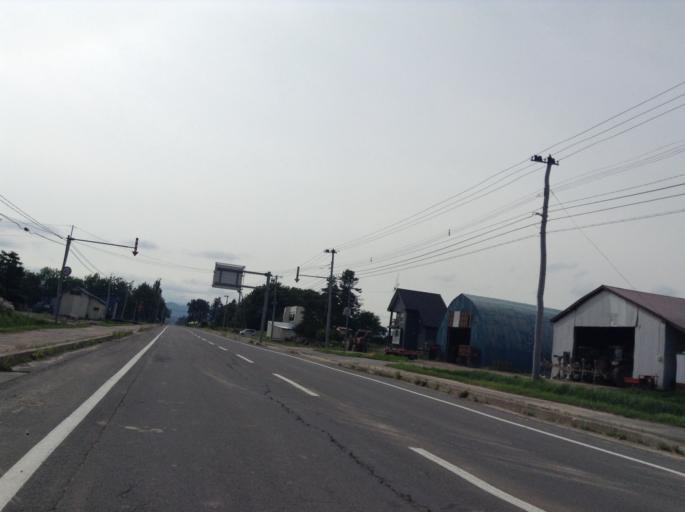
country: JP
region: Hokkaido
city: Nayoro
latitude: 44.4377
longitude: 142.4004
